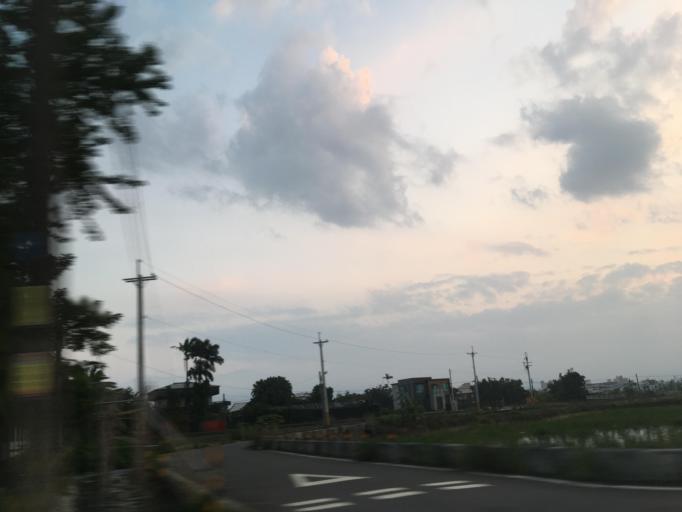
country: TW
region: Taiwan
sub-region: Yilan
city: Yilan
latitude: 24.6913
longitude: 121.7841
